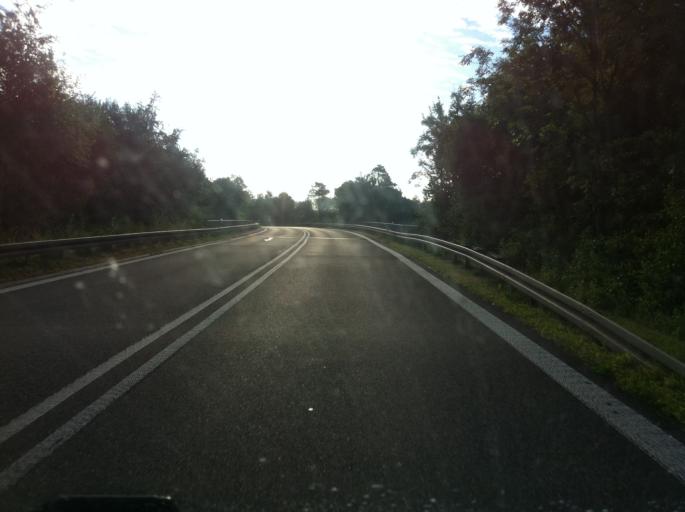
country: DE
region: North Rhine-Westphalia
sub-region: Regierungsbezirk Koln
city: Nettersheim
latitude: 50.5265
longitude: 6.6684
